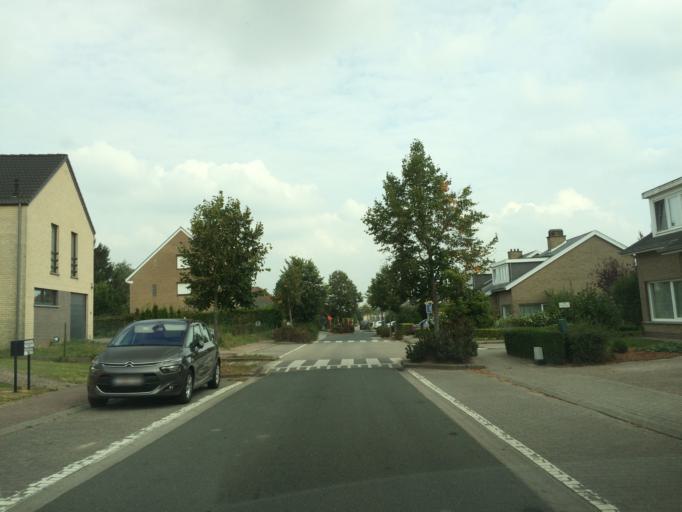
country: BE
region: Flanders
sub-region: Provincie Vlaams-Brabant
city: Wemmel
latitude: 50.9039
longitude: 4.2906
